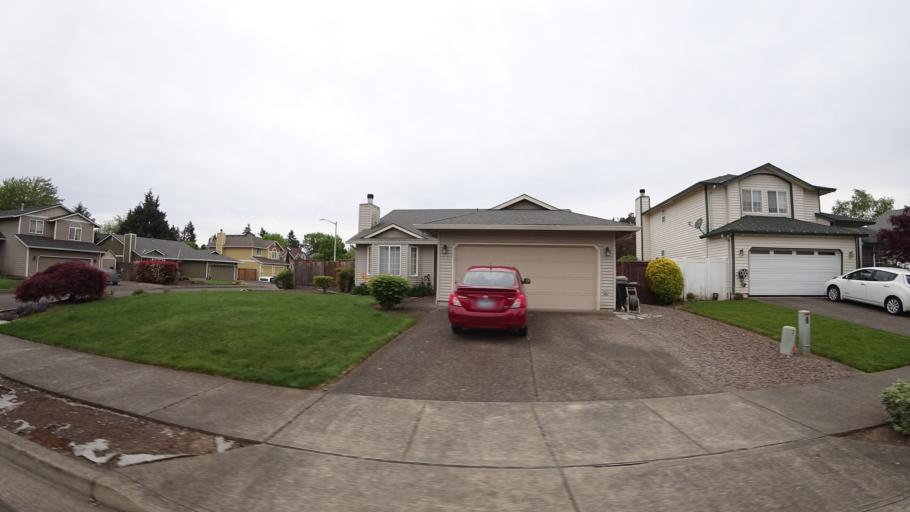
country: US
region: Oregon
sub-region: Washington County
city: Hillsboro
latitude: 45.5051
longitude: -122.9294
